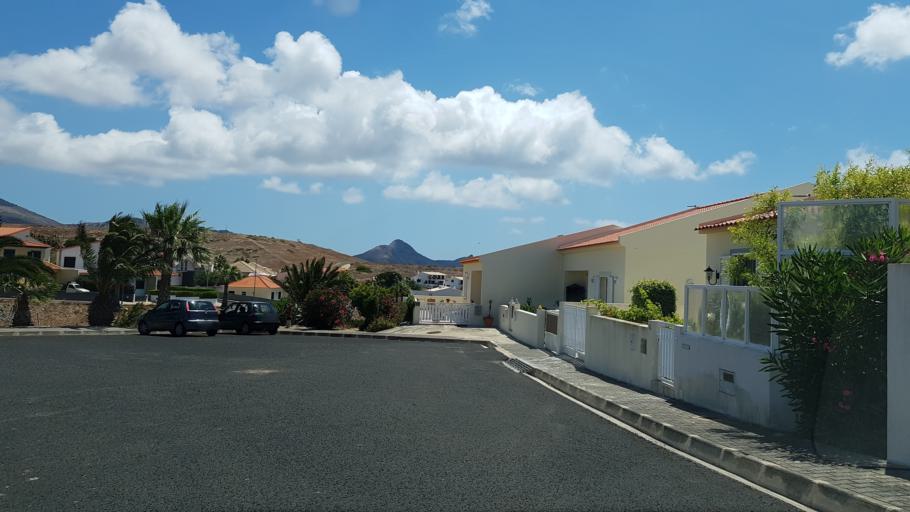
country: PT
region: Madeira
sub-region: Porto Santo
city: Vila de Porto Santo
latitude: 33.0548
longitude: -16.3547
